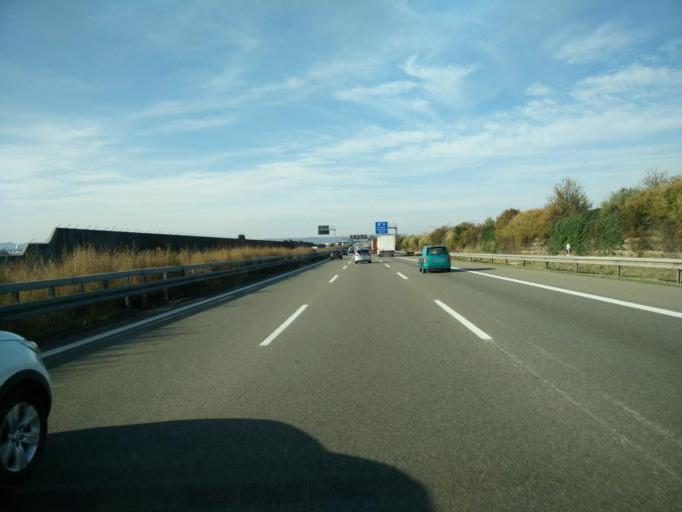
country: DE
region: Baden-Wuerttemberg
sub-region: Regierungsbezirk Stuttgart
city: Ostfildern
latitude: 48.6972
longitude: 9.2422
